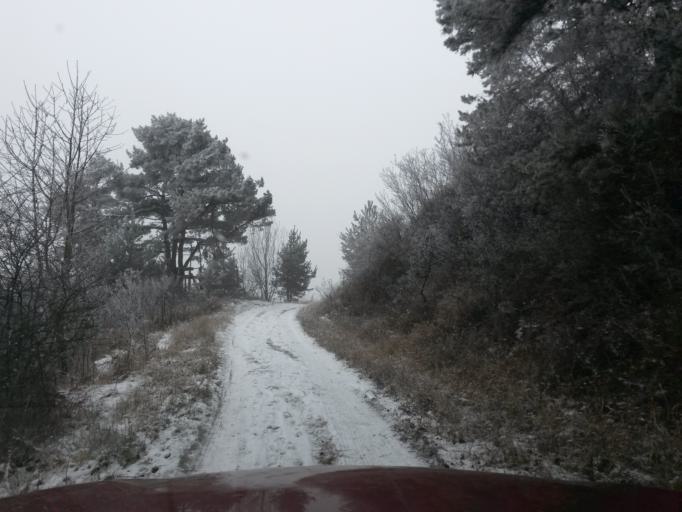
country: SK
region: Kosicky
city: Krompachy
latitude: 48.9707
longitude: 20.9787
